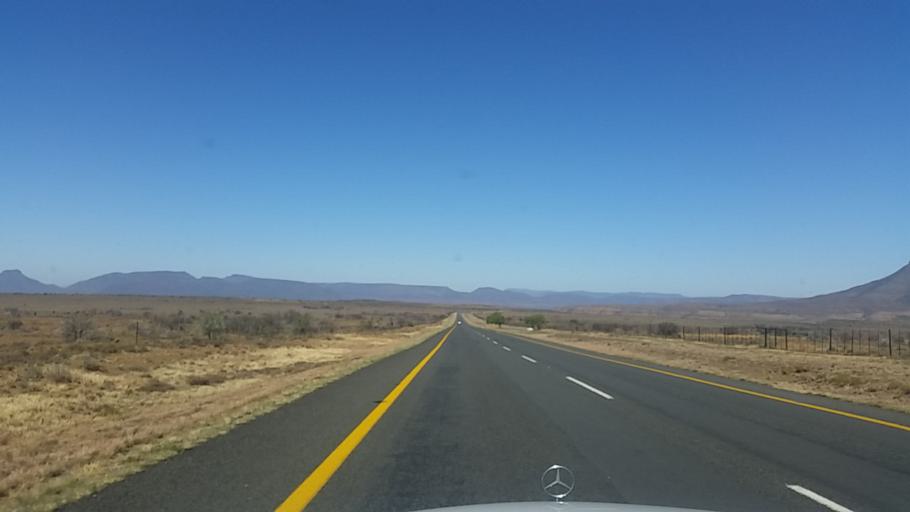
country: ZA
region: Eastern Cape
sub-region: Cacadu District Municipality
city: Graaff-Reinet
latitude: -32.1221
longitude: 24.6018
